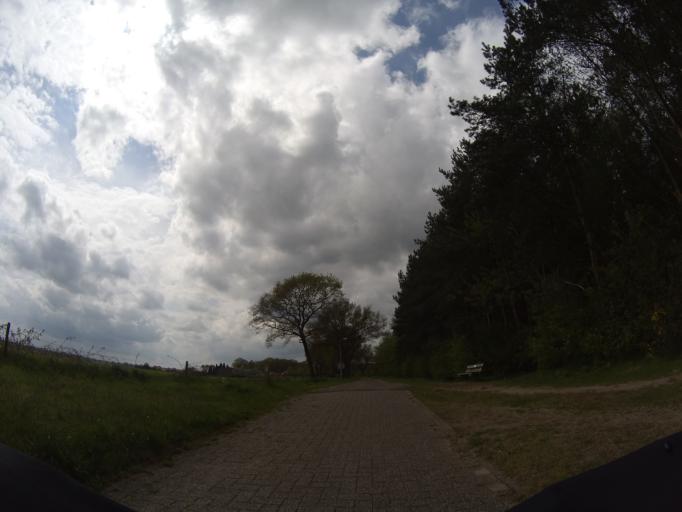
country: NL
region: Overijssel
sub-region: Gemeente Twenterand
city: Magele
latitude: 52.5283
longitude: 6.5530
